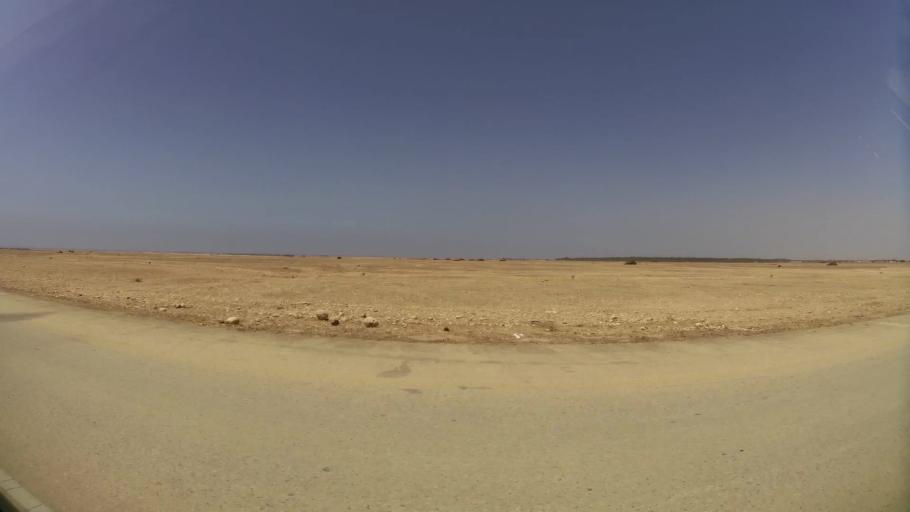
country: OM
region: Zufar
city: Salalah
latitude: 17.0469
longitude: 54.2419
